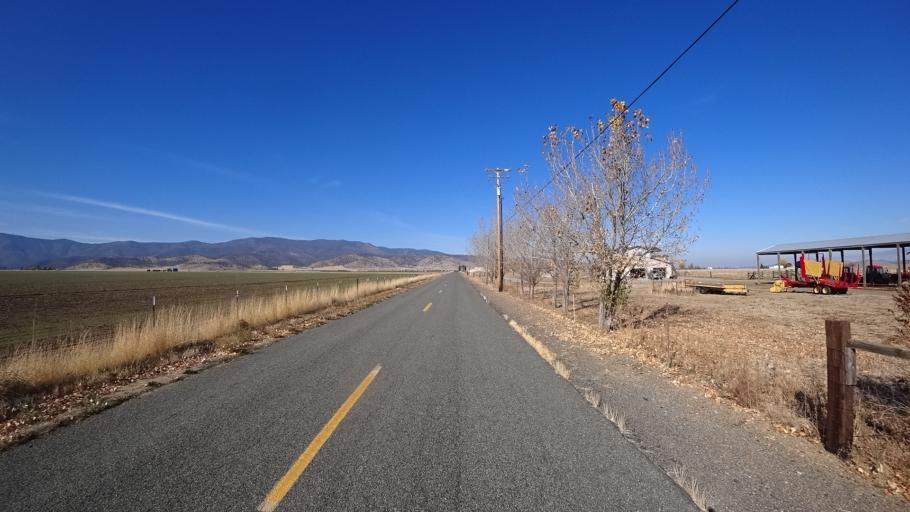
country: US
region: California
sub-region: Siskiyou County
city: Montague
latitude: 41.5431
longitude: -122.5388
